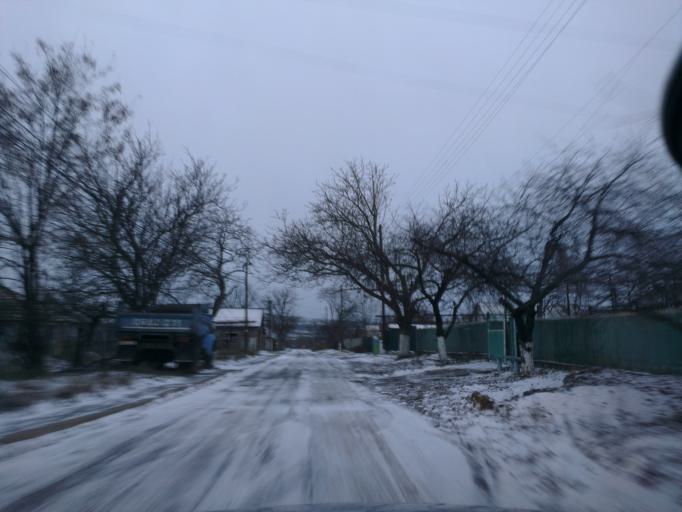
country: MD
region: Chisinau
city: Ciorescu
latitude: 47.1163
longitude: 28.9017
